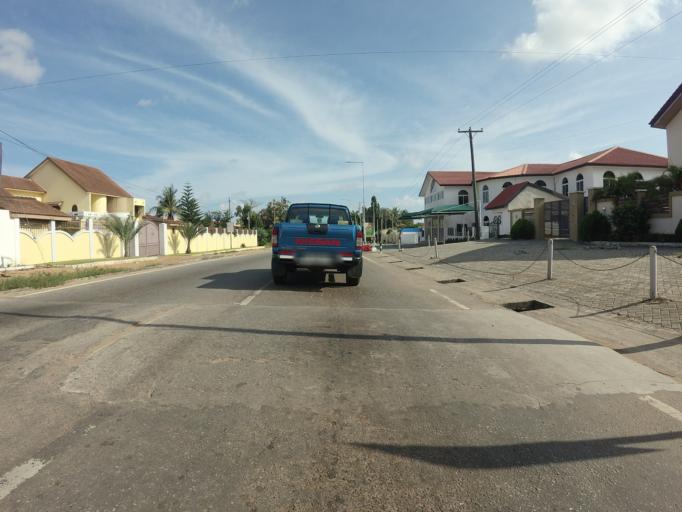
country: GH
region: Greater Accra
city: Medina Estates
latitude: 5.6374
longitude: -0.1617
